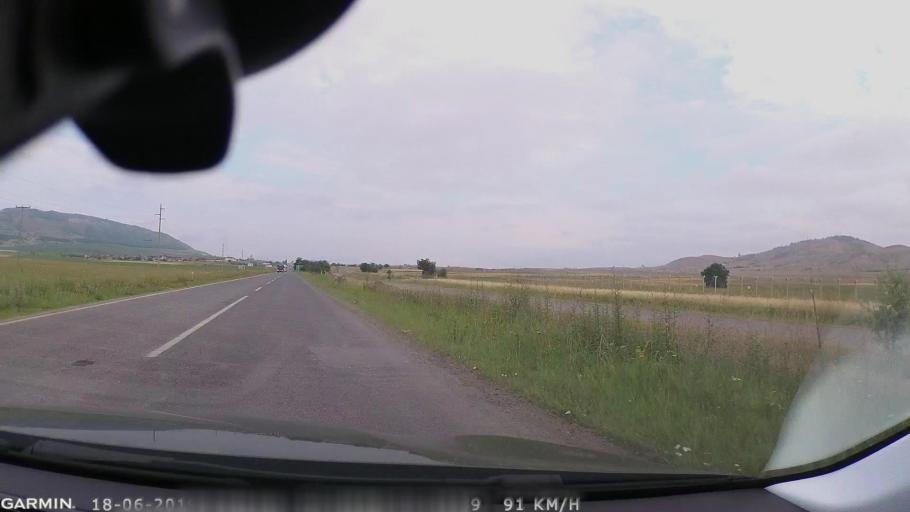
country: MK
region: Stip
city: Shtip
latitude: 41.7682
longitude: 22.1515
